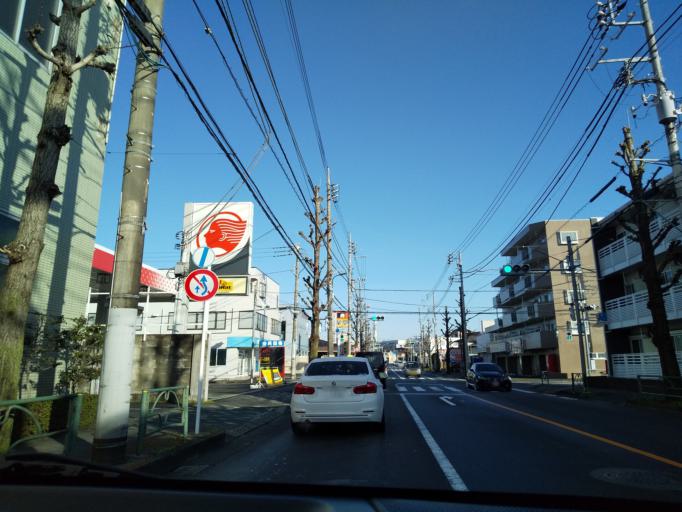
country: JP
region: Tokyo
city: Hachioji
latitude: 35.6603
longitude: 139.3592
